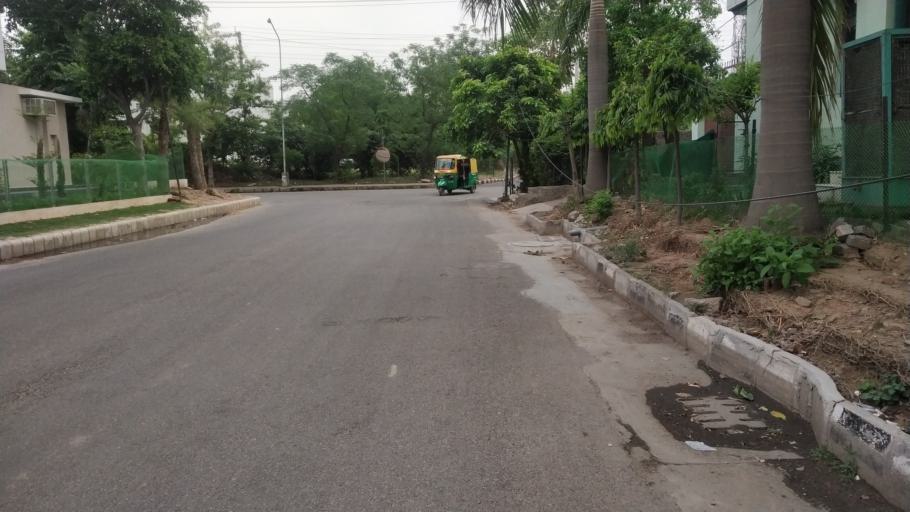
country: IN
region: Punjab
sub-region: Ajitgarh
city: Mohali
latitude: 30.7028
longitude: 76.7141
